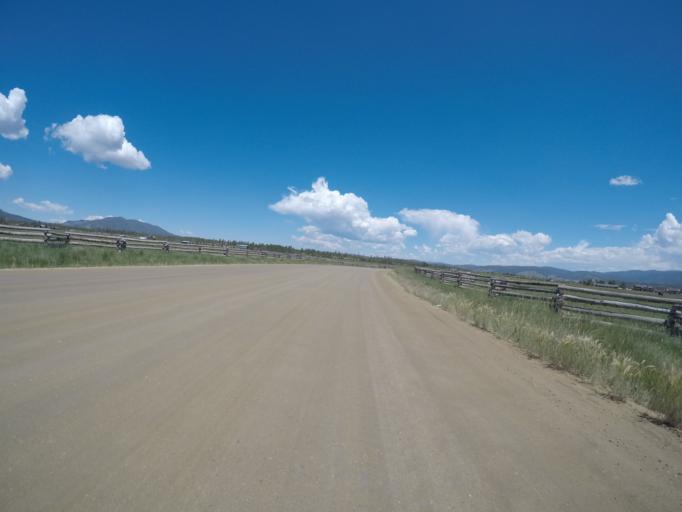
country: US
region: Colorado
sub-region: Grand County
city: Fraser
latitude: 39.9410
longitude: -105.8224
